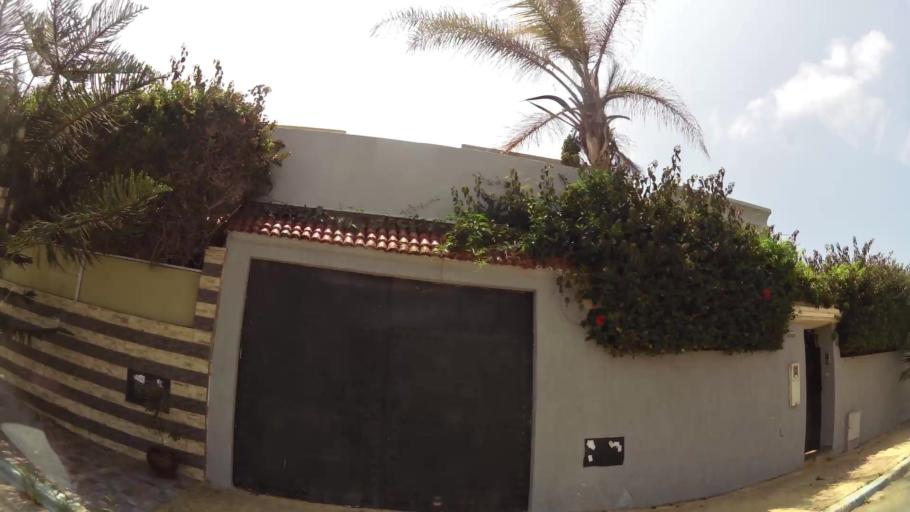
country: MA
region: Rabat-Sale-Zemmour-Zaer
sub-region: Skhirate-Temara
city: Temara
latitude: 33.9713
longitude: -6.9027
